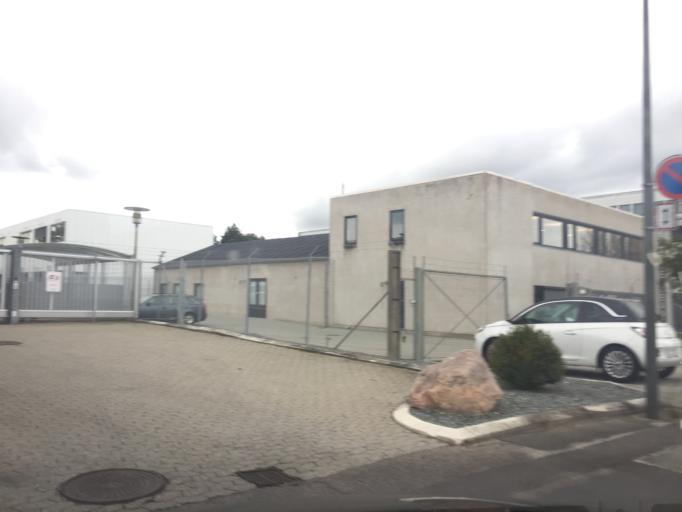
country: DK
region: Capital Region
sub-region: Herlev Kommune
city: Herlev
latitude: 55.7176
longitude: 12.4321
